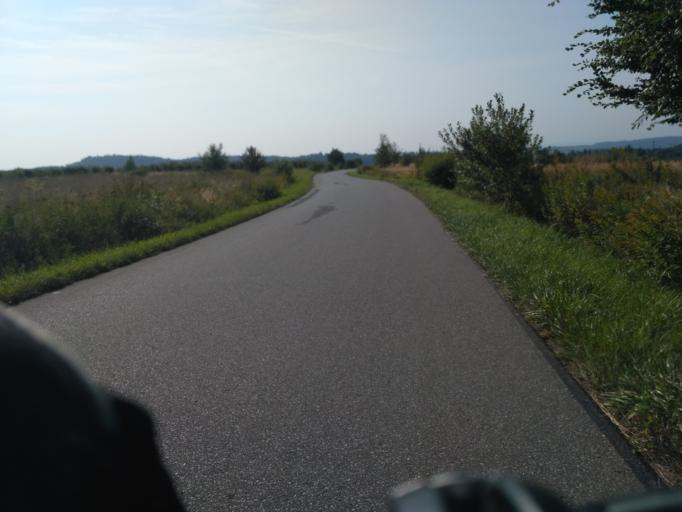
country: PL
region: Subcarpathian Voivodeship
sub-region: Powiat brzozowski
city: Golcowa
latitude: 49.7999
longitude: 22.0254
